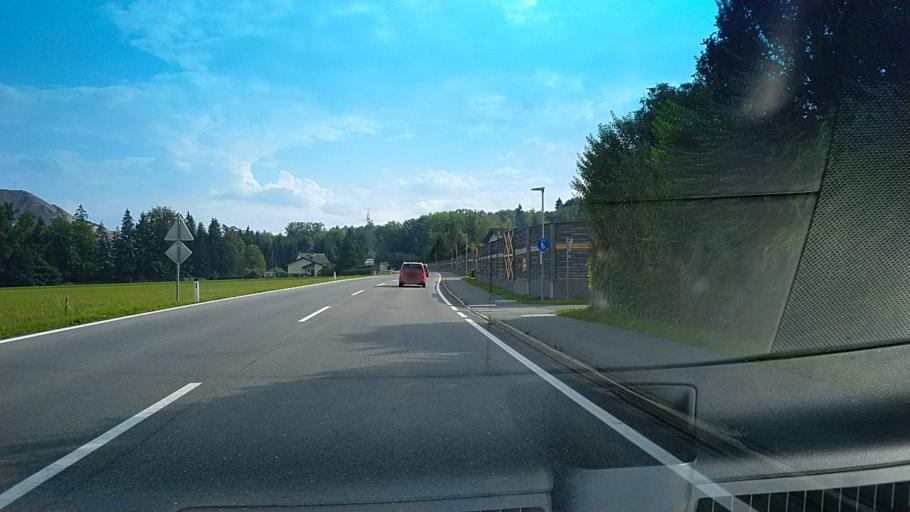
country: AT
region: Styria
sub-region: Politischer Bezirk Deutschlandsberg
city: Hollenegg
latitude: 46.7986
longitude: 15.2203
